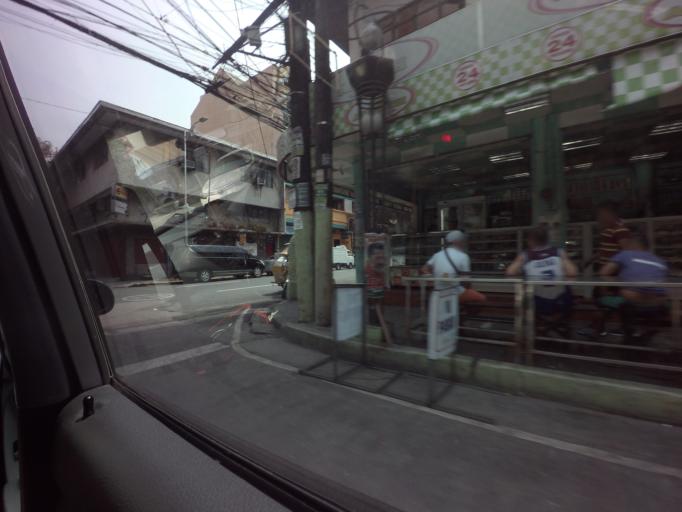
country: PH
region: Metro Manila
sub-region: City of Manila
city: Port Area
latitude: 14.5728
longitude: 120.9912
